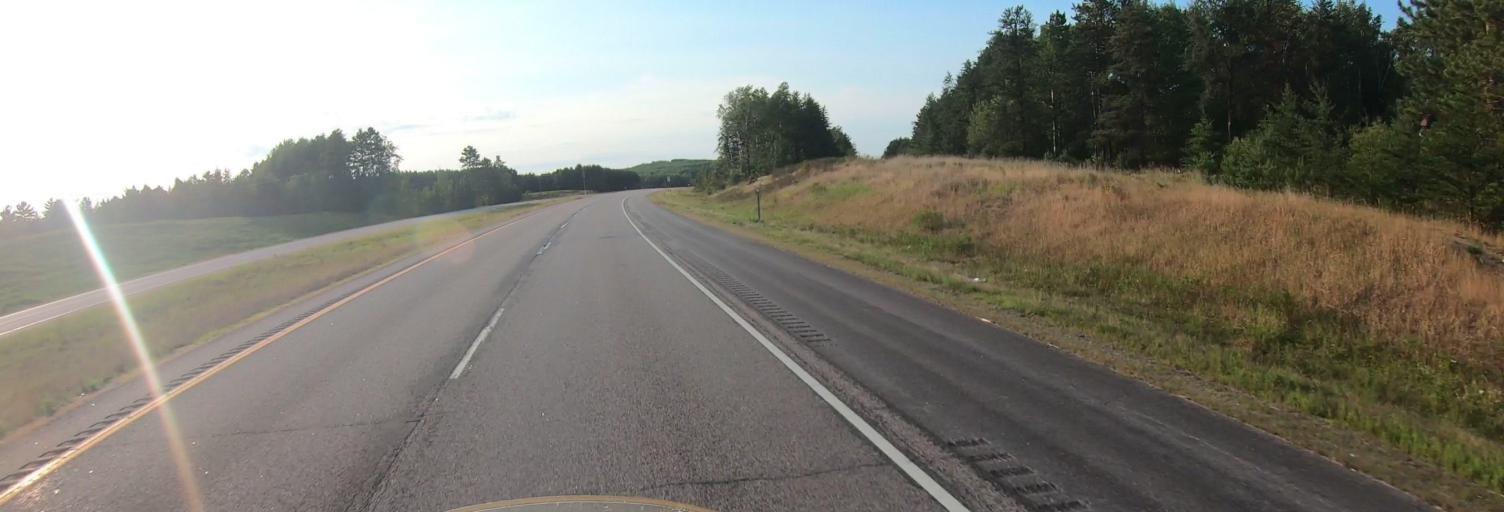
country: US
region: Minnesota
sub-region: Saint Louis County
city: Mountain Iron
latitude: 47.6730
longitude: -92.6327
